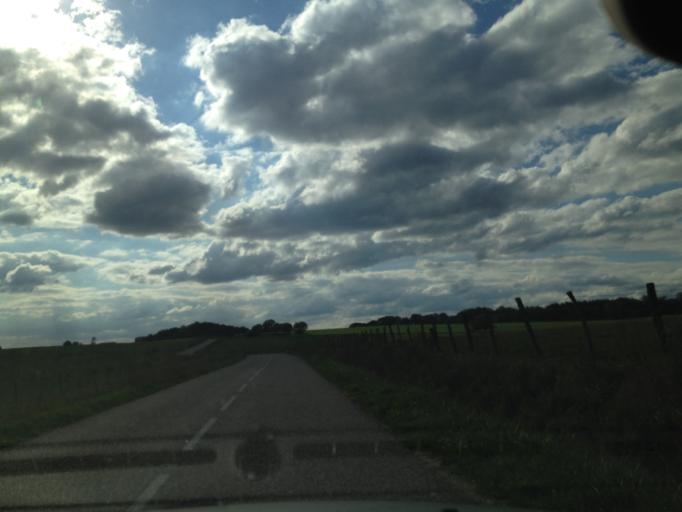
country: FR
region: Franche-Comte
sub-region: Departement de la Haute-Saone
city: Faverney
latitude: 47.7894
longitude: 6.0276
